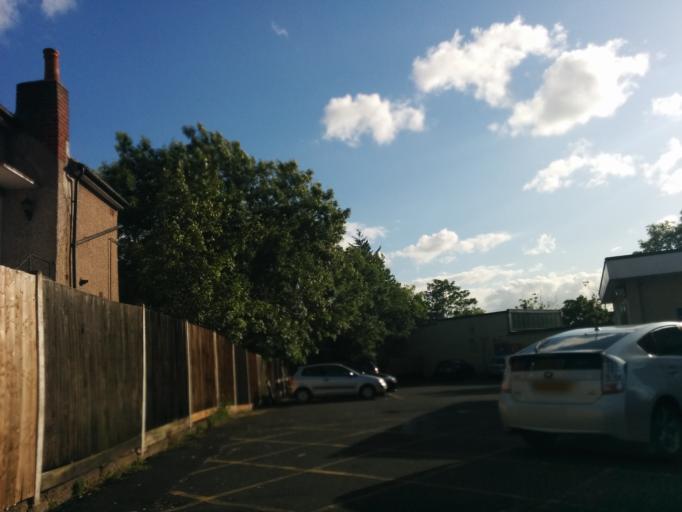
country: GB
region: England
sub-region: Greater London
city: Greenhill
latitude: 51.5717
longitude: -0.3532
